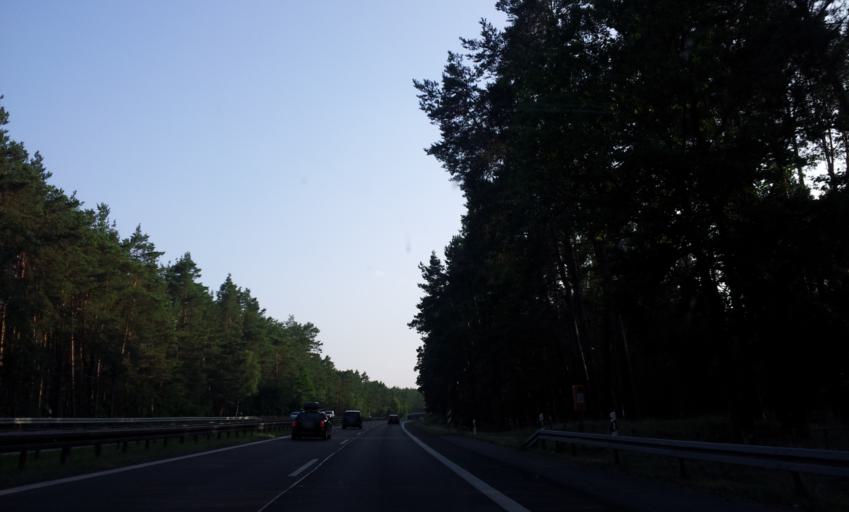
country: DE
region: Brandenburg
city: Marienwerder
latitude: 52.8338
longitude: 13.6602
